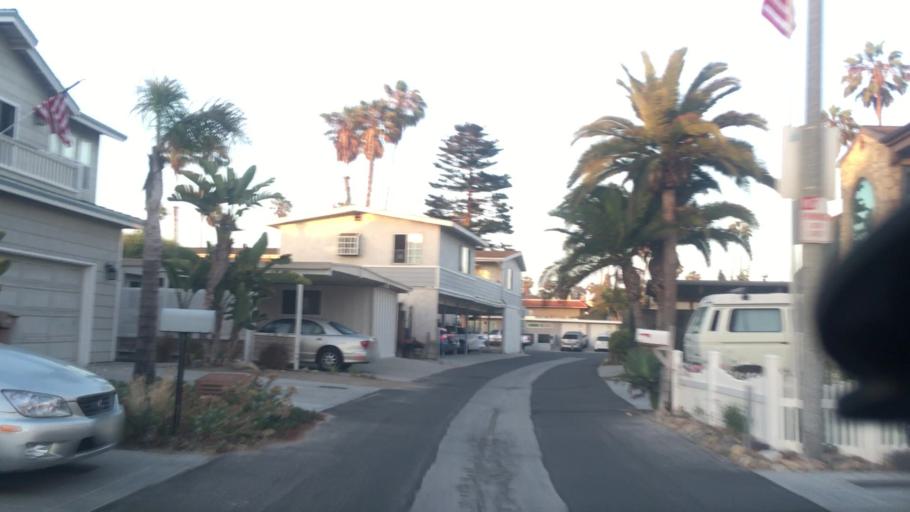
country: US
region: California
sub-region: Ventura County
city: Ventura
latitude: 34.2570
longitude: -119.2688
